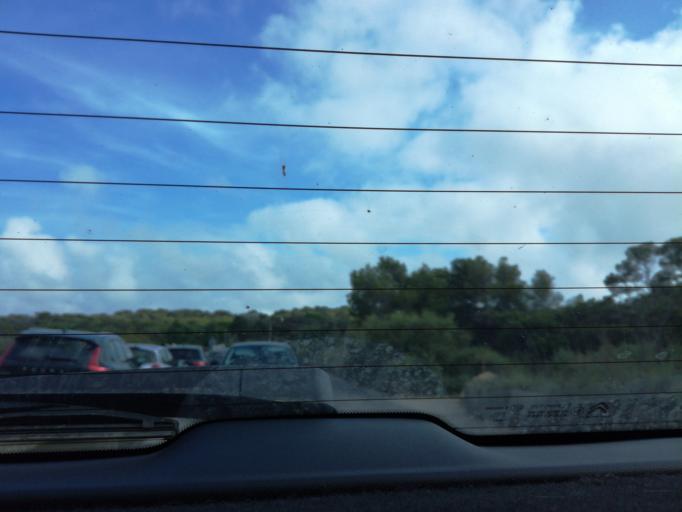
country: FR
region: Provence-Alpes-Cote d'Azur
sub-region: Departement du Var
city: Hyeres
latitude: 43.0458
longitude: 6.1341
